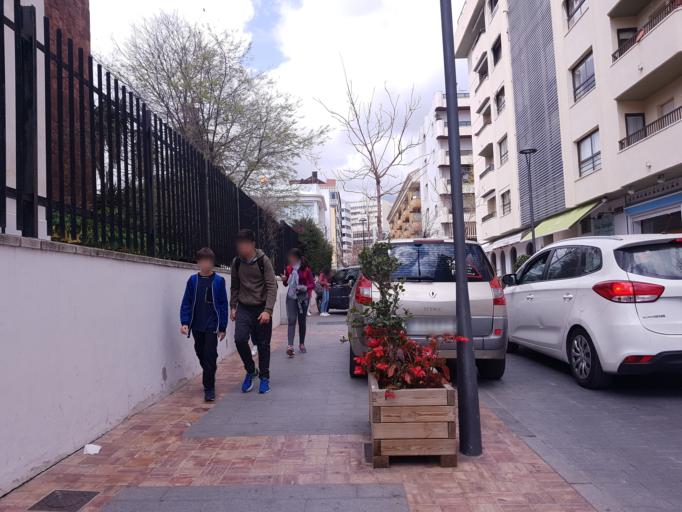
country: ES
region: Andalusia
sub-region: Provincia de Malaga
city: Marbella
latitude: 36.5081
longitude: -4.8885
